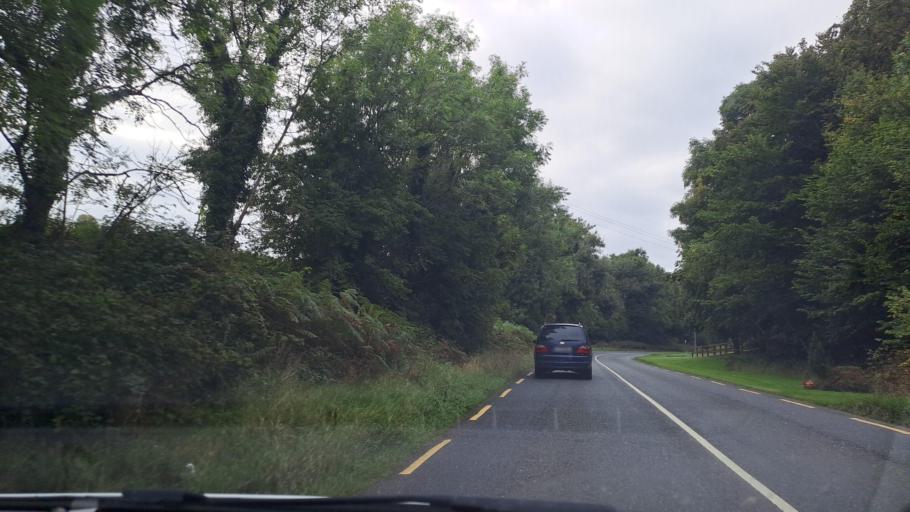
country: IE
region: Ulster
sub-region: County Monaghan
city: Carrickmacross
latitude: 54.0088
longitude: -6.7489
